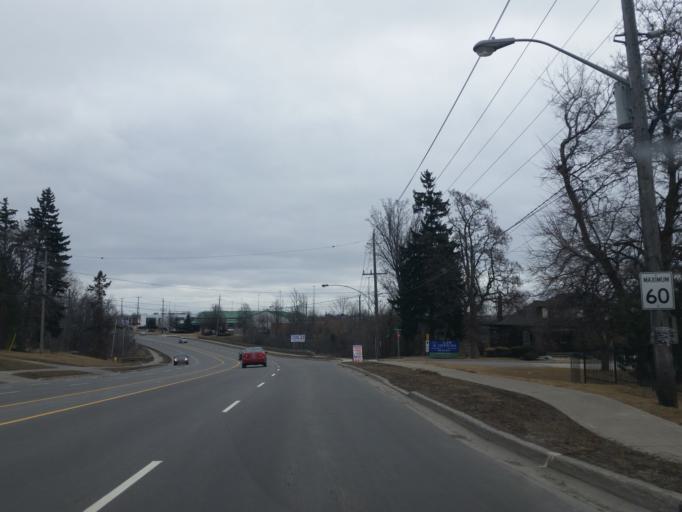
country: CA
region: Ontario
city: Pickering
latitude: 43.8103
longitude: -79.1273
